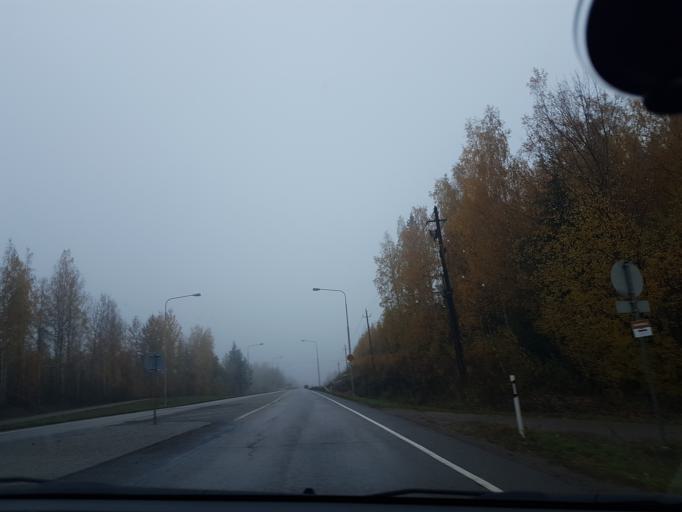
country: FI
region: Uusimaa
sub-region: Helsinki
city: Jaervenpaeae
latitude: 60.4518
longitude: 25.1360
